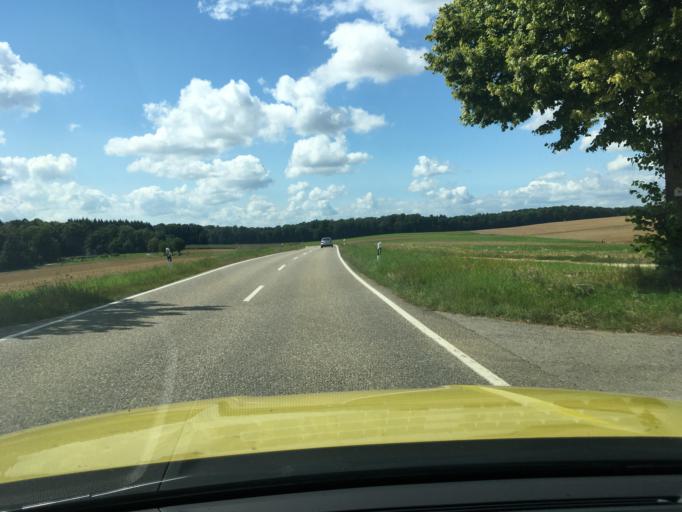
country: DE
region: Baden-Wuerttemberg
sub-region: Regierungsbezirk Stuttgart
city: Massenbachhausen
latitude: 49.1728
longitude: 9.0284
